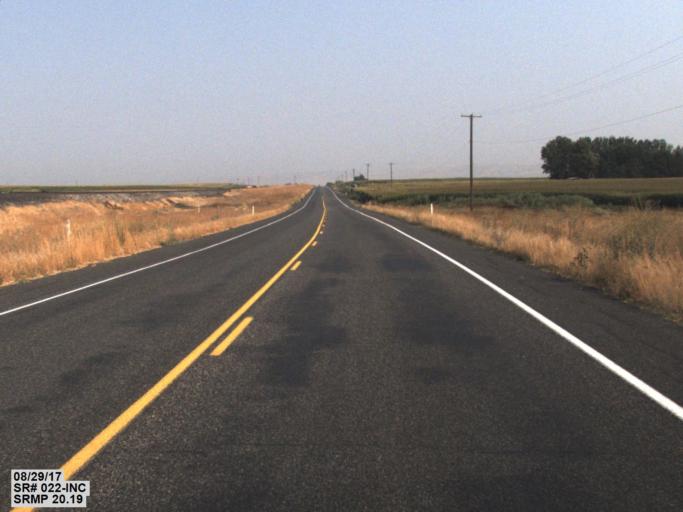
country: US
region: Washington
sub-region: Yakima County
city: Mabton
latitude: 46.2258
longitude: -120.0573
